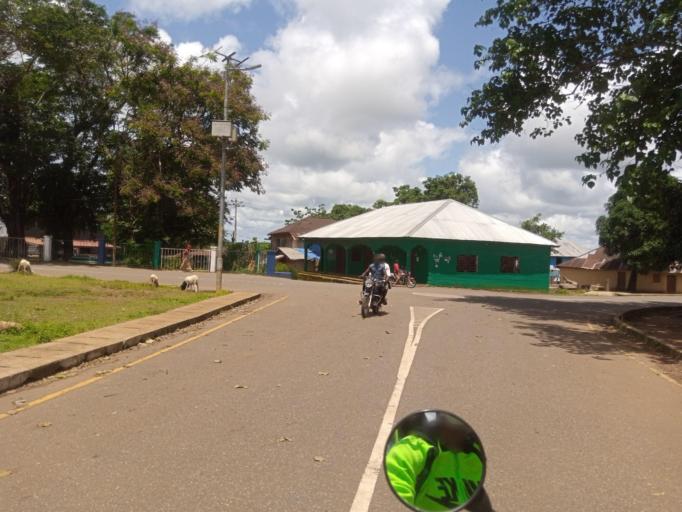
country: SL
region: Northern Province
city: Port Loko
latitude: 8.7653
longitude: -12.7888
